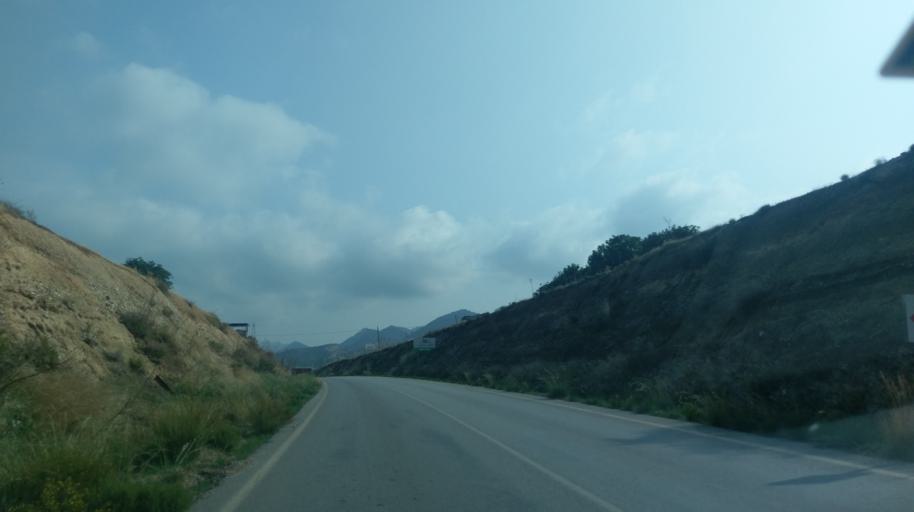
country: CY
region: Ammochostos
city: Lefkonoiko
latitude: 35.3526
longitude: 33.6245
